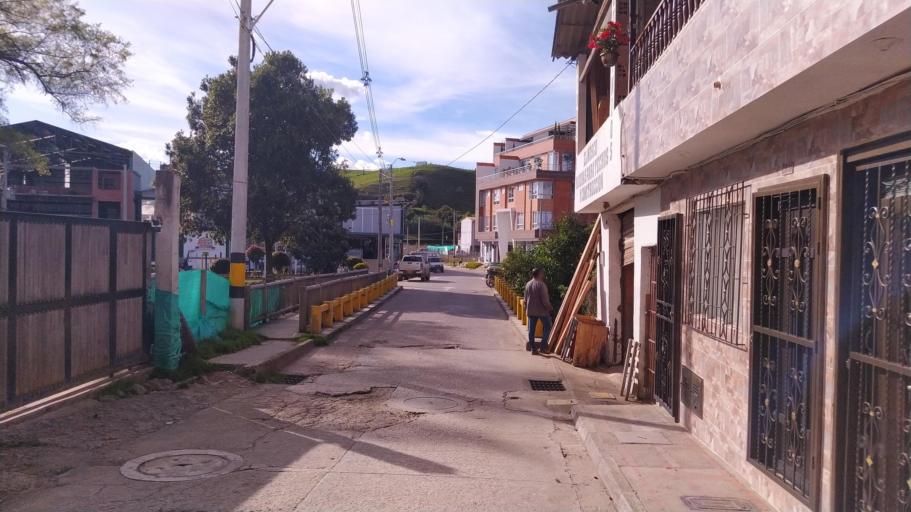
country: CO
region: Antioquia
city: Entrerrios
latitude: 6.5679
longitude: -75.5170
